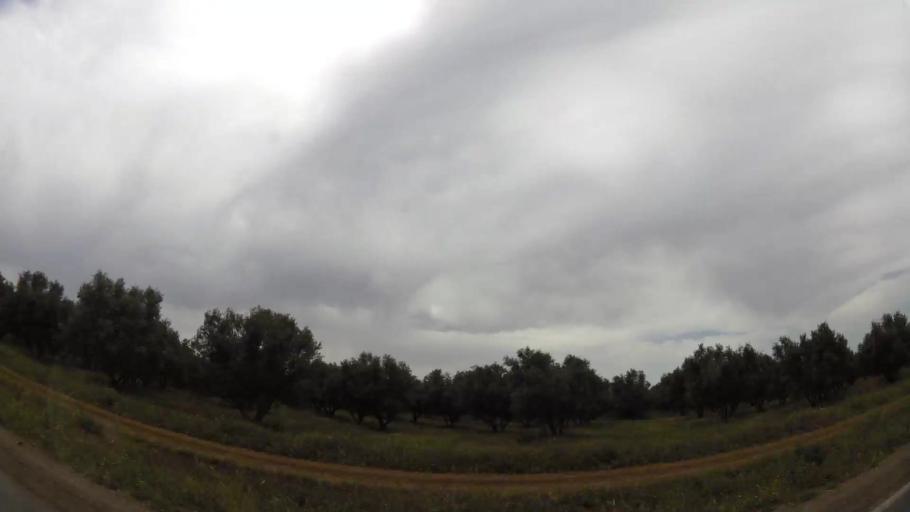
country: MA
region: Rabat-Sale-Zemmour-Zaer
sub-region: Khemisset
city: Tiflet
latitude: 33.8157
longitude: -6.2725
